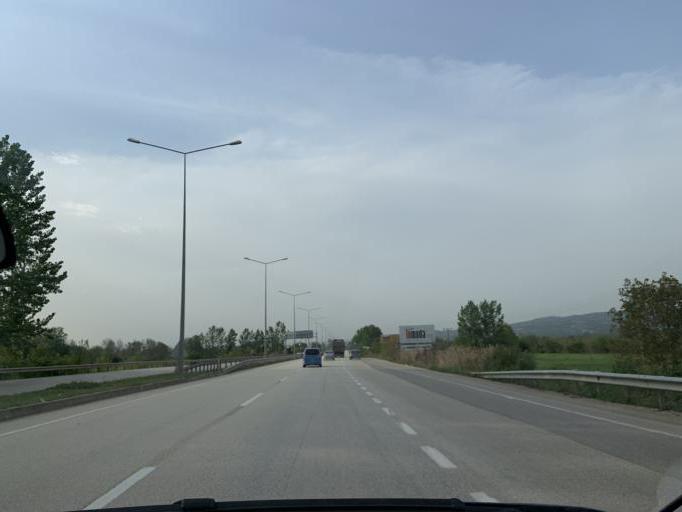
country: TR
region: Bursa
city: Kursunlu
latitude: 40.0442
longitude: 29.5915
